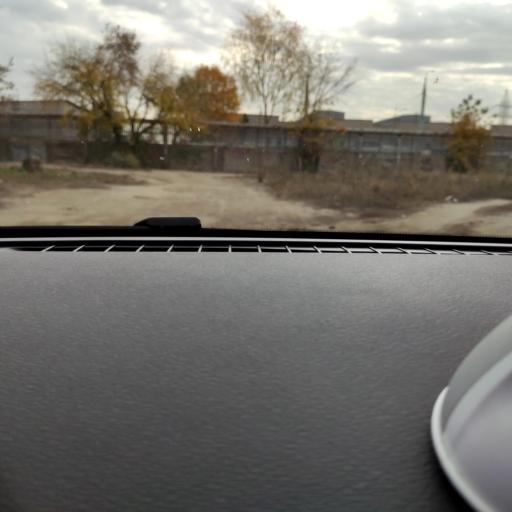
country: RU
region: Samara
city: Samara
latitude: 53.2348
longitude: 50.2029
